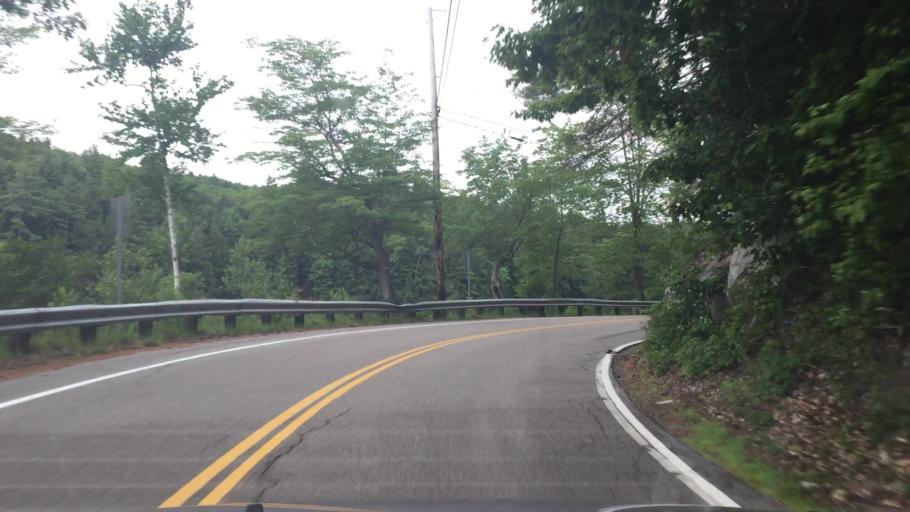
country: US
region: New Hampshire
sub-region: Carroll County
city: Madison
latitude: 43.8863
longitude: -71.0755
